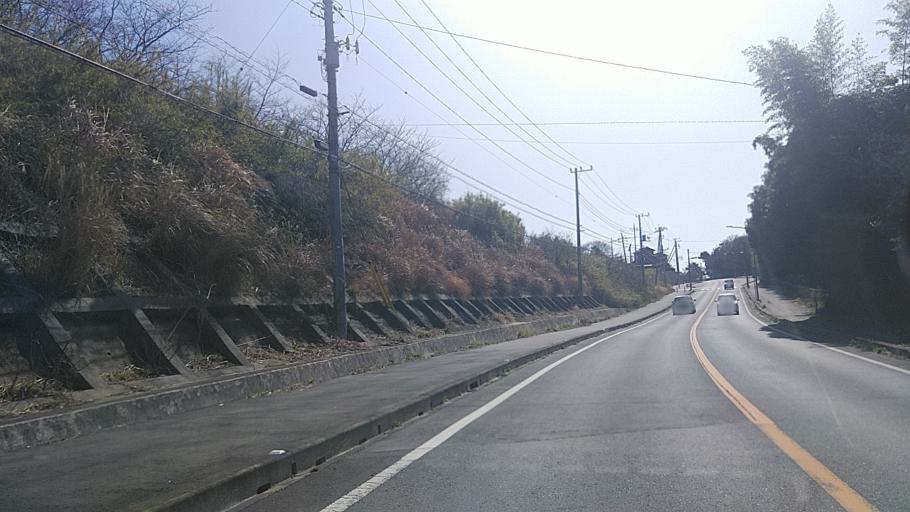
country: JP
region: Ibaraki
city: Toride
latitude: 35.8900
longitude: 140.0978
